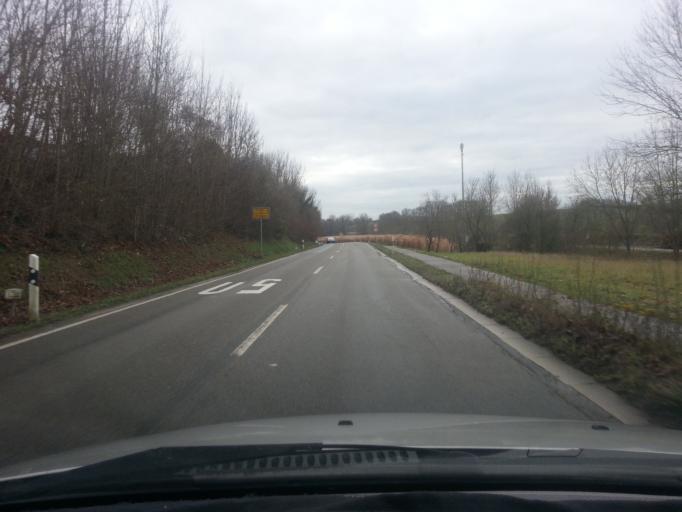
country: DE
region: Baden-Wuerttemberg
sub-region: Regierungsbezirk Stuttgart
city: Ittlingen
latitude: 49.1863
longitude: 8.9353
